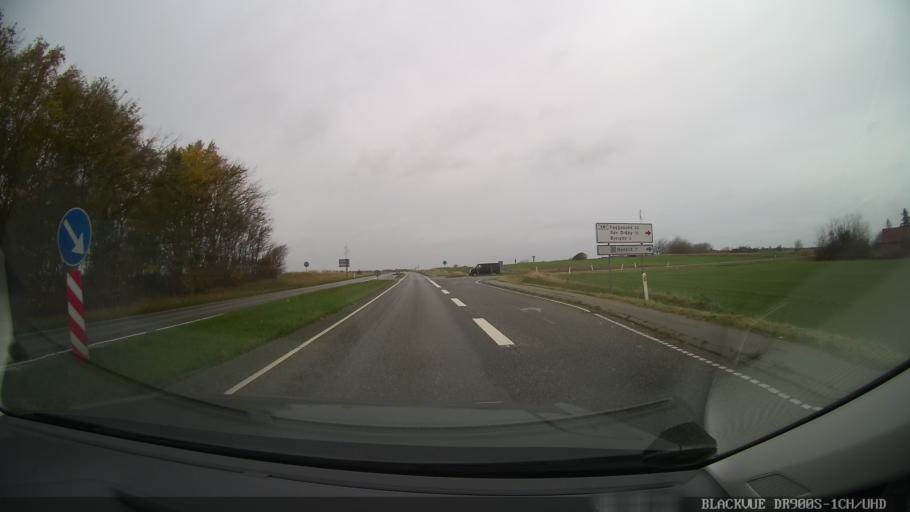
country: DK
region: North Denmark
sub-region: Thisted Kommune
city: Thisted
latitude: 56.8548
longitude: 8.6974
